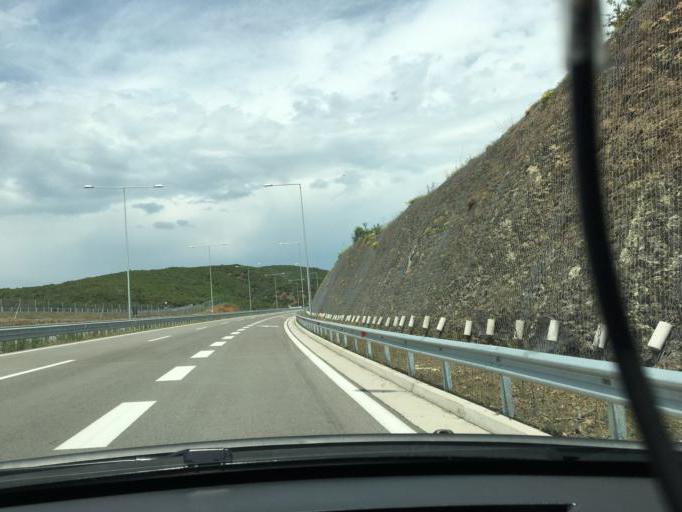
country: MK
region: Gevgelija
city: Miravci
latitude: 41.2990
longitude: 22.4296
